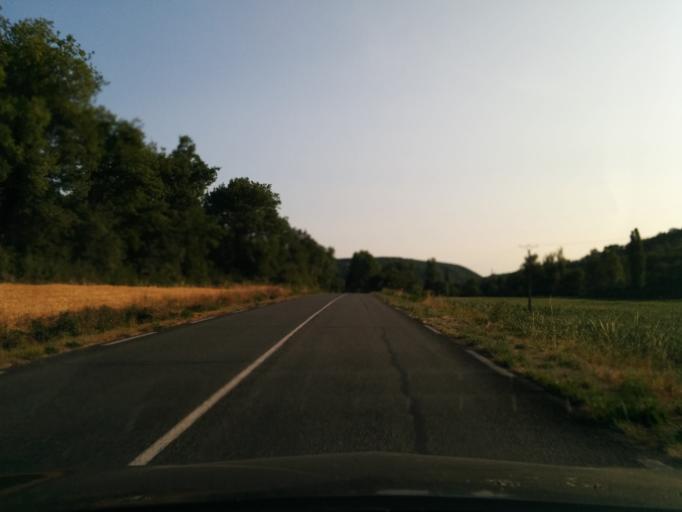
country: FR
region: Midi-Pyrenees
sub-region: Departement du Lot
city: Le Vigan
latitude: 44.6832
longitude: 1.4841
